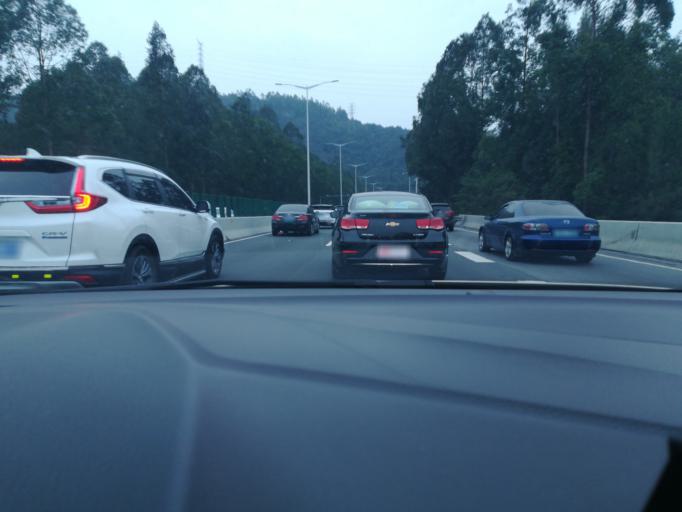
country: CN
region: Guangdong
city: Longdong
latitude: 23.2248
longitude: 113.3568
